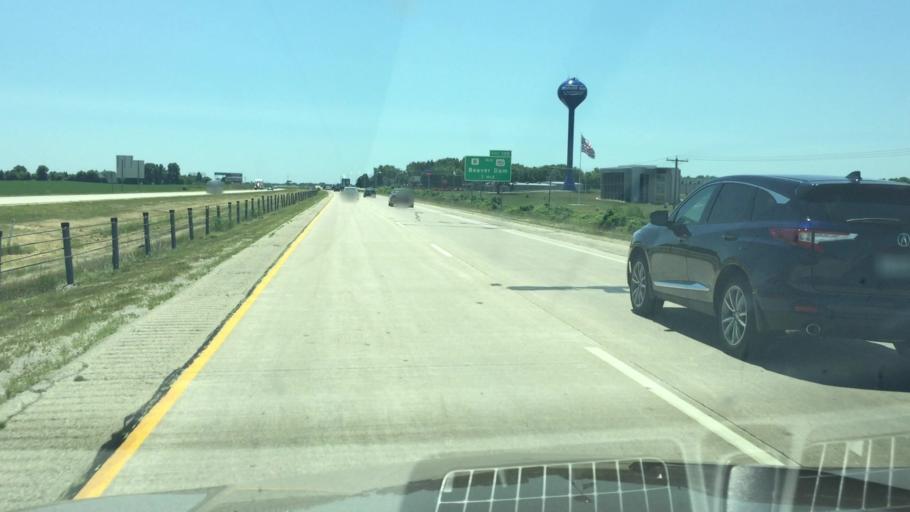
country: US
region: Wisconsin
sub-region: Dodge County
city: Beaver Dam
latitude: 43.5002
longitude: -88.8102
